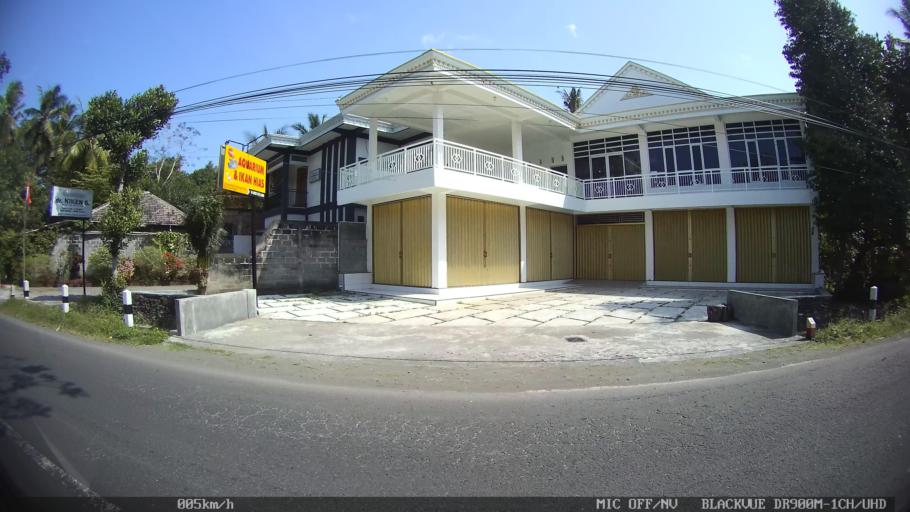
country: ID
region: Daerah Istimewa Yogyakarta
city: Srandakan
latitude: -7.9443
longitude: 110.2282
